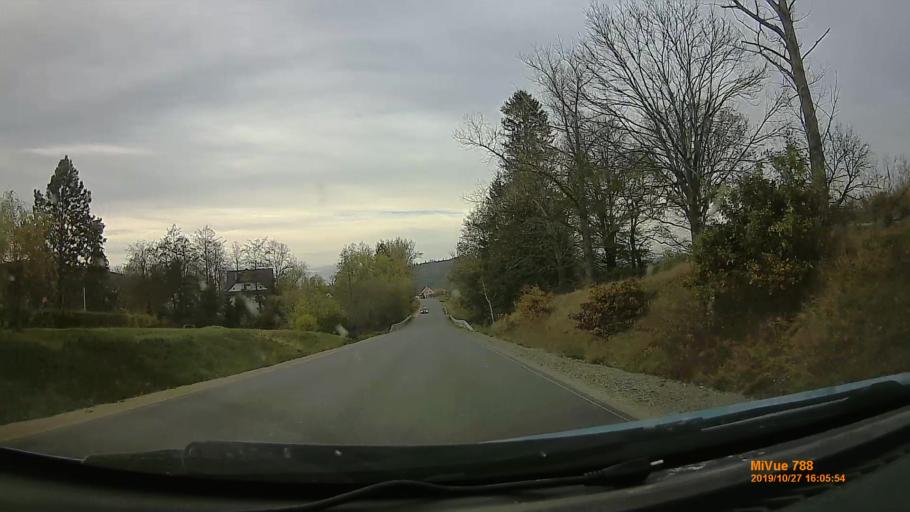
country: PL
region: Lower Silesian Voivodeship
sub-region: Powiat klodzki
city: Nowa Ruda
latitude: 50.5350
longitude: 16.4791
